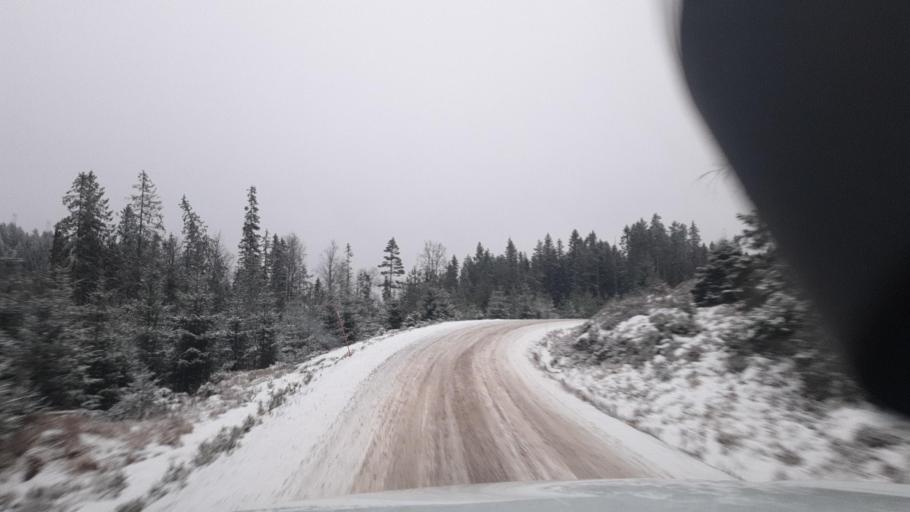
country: SE
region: Vaermland
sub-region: Eda Kommun
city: Charlottenberg
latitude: 60.0633
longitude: 12.5331
